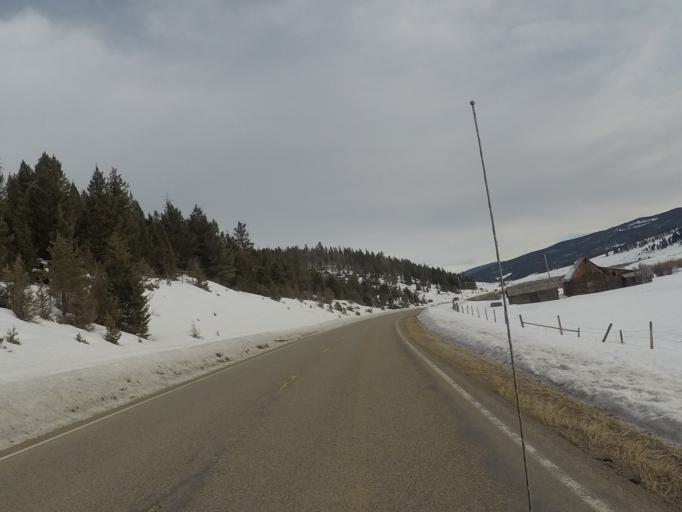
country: US
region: Montana
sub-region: Meagher County
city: White Sulphur Springs
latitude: 46.7052
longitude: -110.8626
